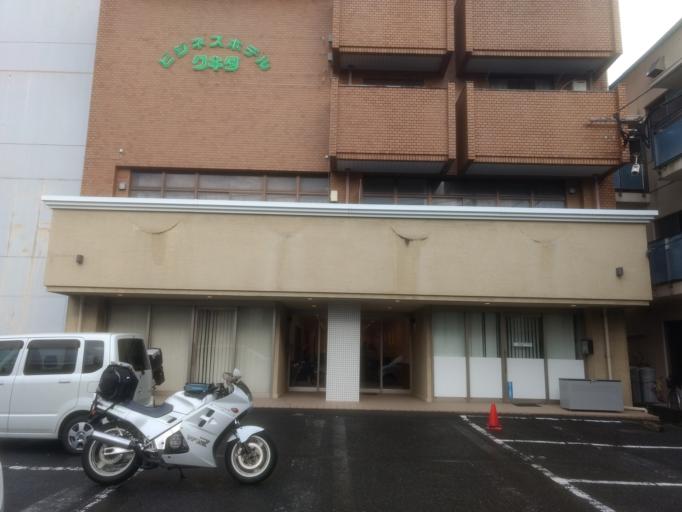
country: JP
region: Kagoshima
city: Kagoshima-shi
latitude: 31.5383
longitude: 130.5351
